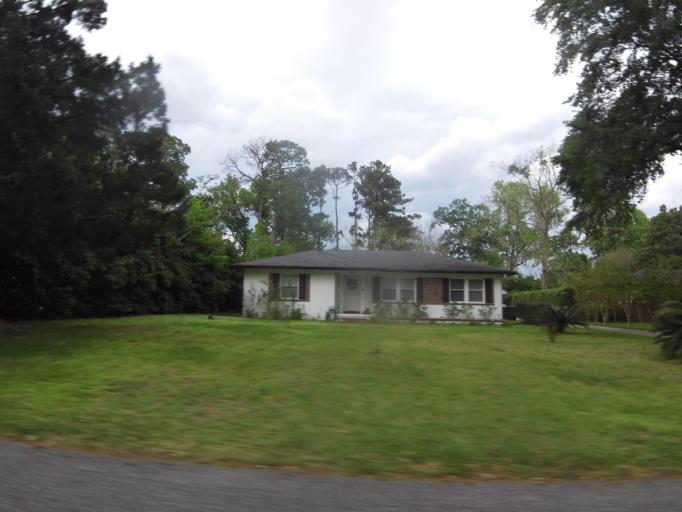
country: US
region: Florida
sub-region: Duval County
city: Jacksonville
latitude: 30.2939
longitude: -81.7336
